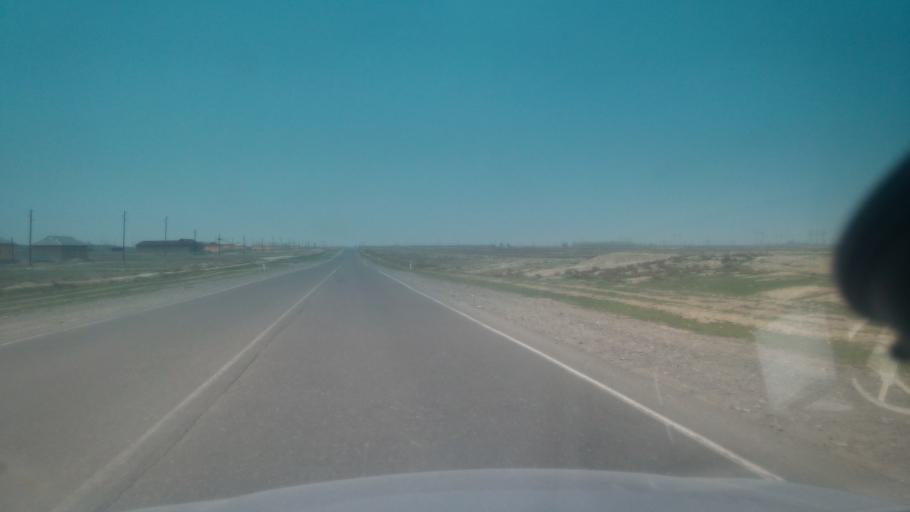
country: UZ
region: Jizzax
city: Dashtobod
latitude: 40.1581
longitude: 68.5688
